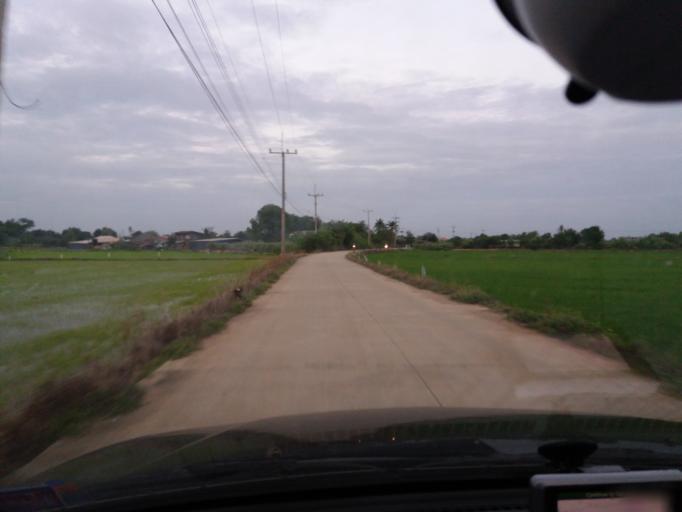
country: TH
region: Suphan Buri
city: Ban Sam Chuk
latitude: 14.7181
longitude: 100.0588
